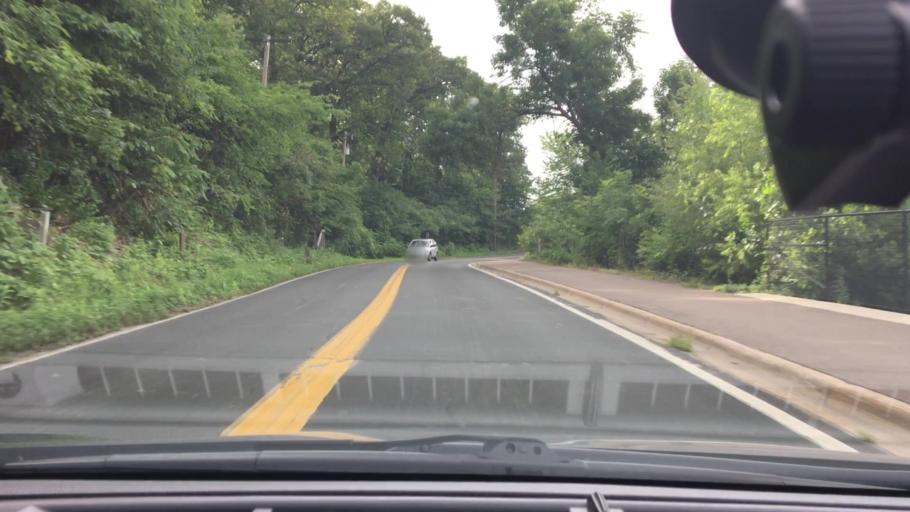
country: US
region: Minnesota
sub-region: Hennepin County
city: Plymouth
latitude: 44.9983
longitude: -93.4282
